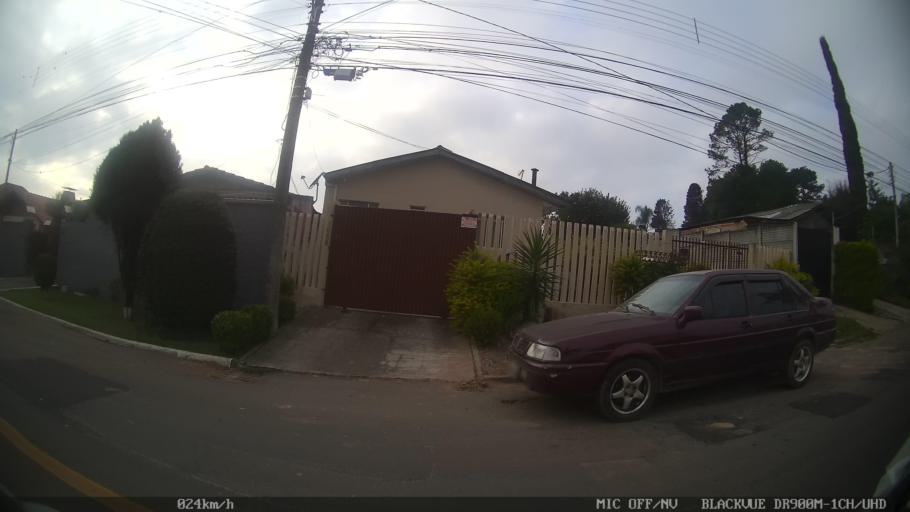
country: BR
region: Parana
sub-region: Almirante Tamandare
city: Almirante Tamandare
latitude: -25.3852
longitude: -49.3366
